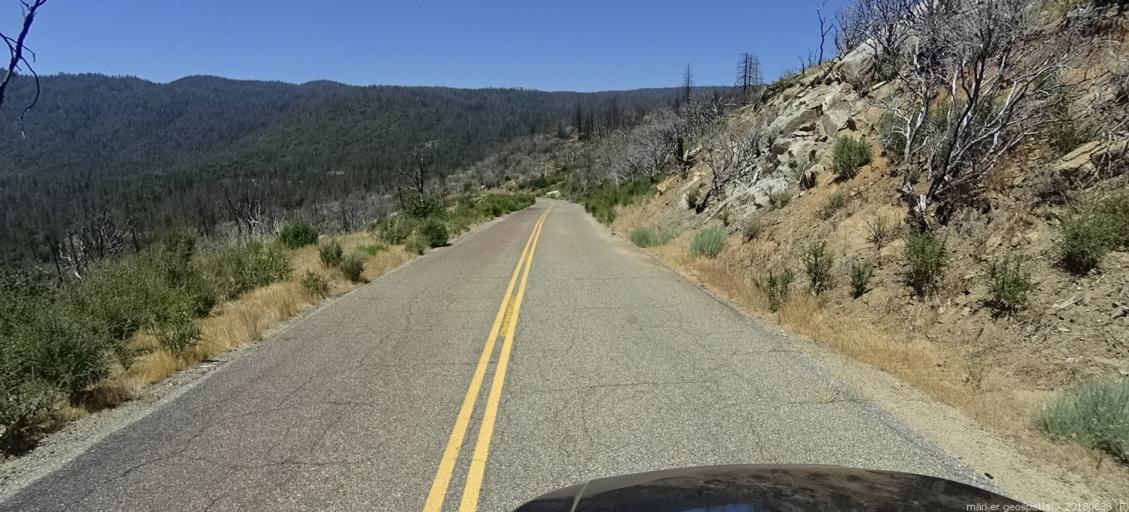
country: US
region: California
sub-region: Fresno County
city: Auberry
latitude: 37.2469
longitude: -119.3513
